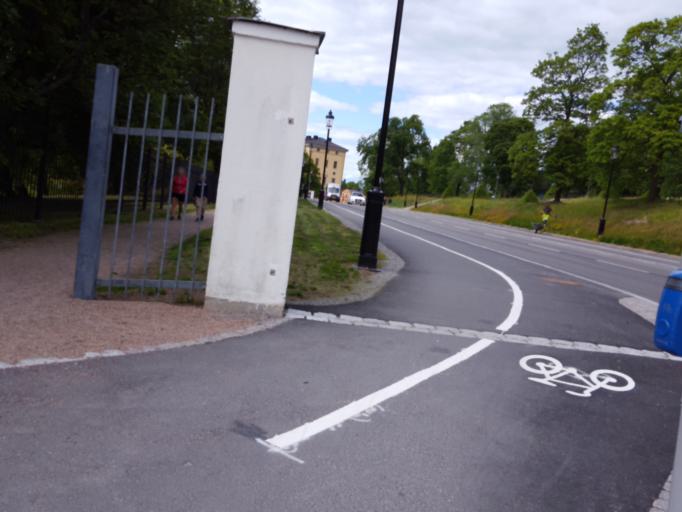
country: SE
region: Uppsala
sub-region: Uppsala Kommun
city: Uppsala
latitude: 59.8524
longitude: 17.6334
